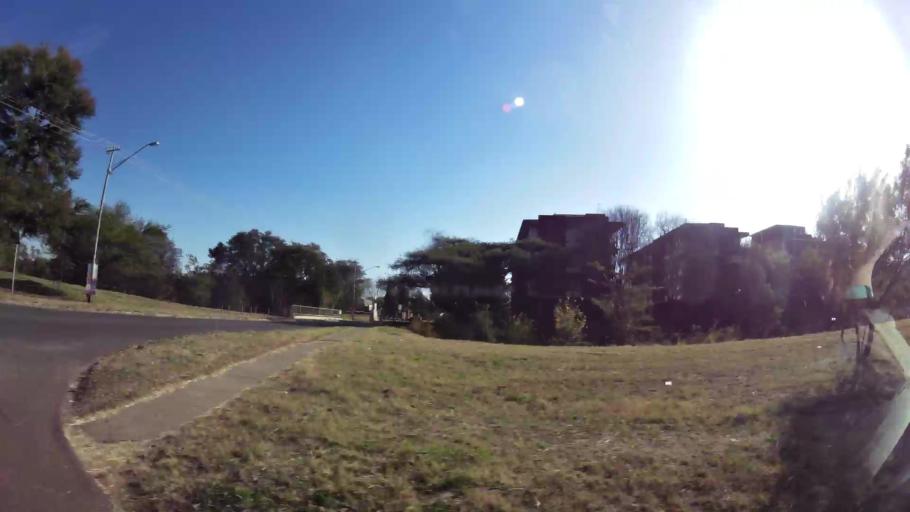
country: ZA
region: Gauteng
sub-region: City of Tshwane Metropolitan Municipality
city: Pretoria
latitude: -25.7205
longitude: 28.2622
